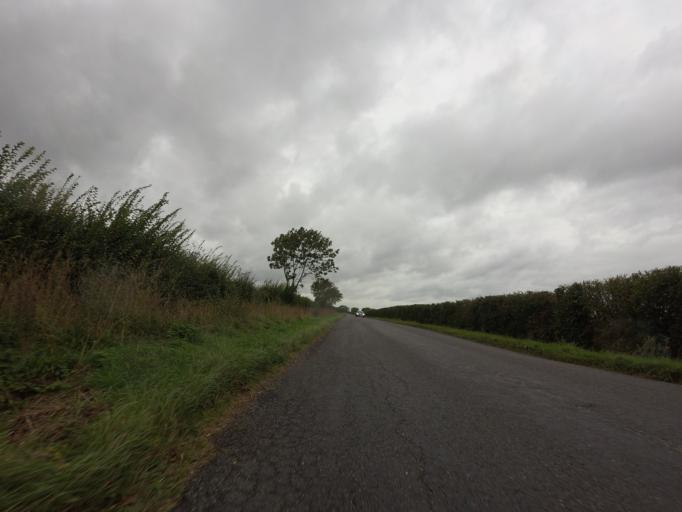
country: GB
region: England
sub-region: Cambridgeshire
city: Haslingfield
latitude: 52.1526
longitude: 0.0431
